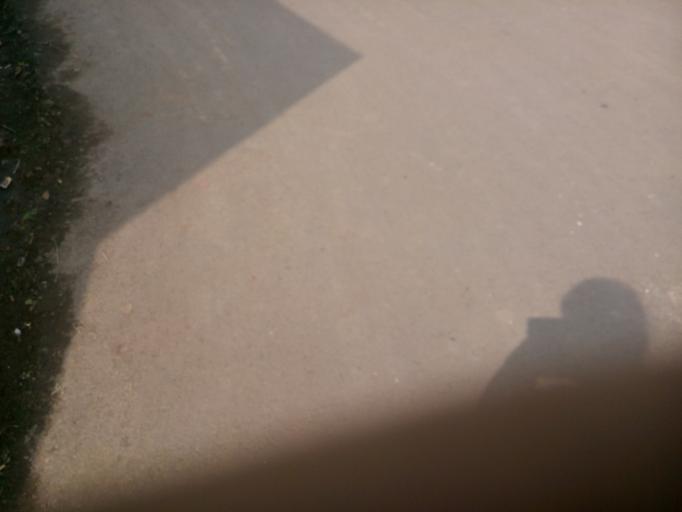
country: IN
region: West Bengal
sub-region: South 24 Paraganas
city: Santoshpur
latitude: 22.4604
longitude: 88.3095
